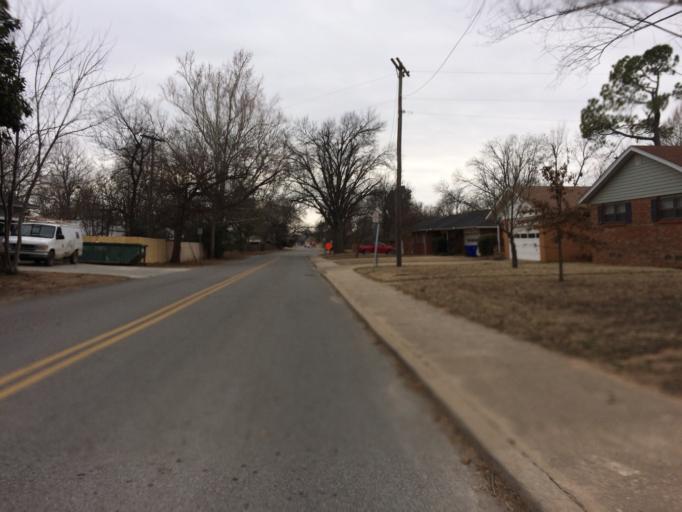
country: US
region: Oklahoma
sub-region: Cleveland County
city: Norman
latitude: 35.2084
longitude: -97.4634
